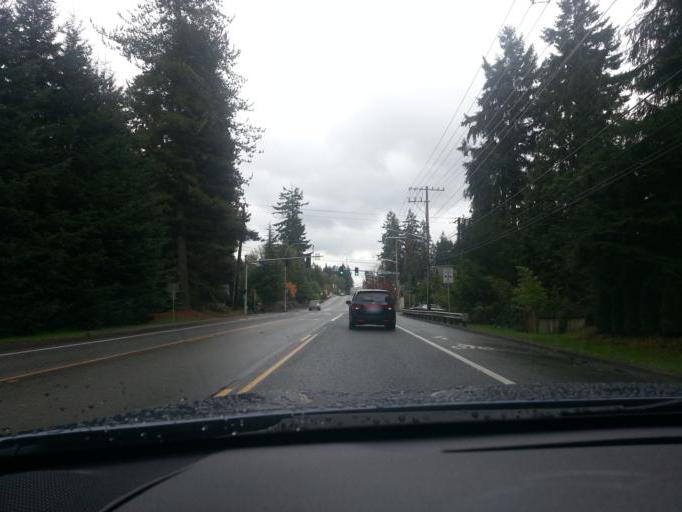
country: US
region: Washington
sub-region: Snohomish County
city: North Creek
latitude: 47.7911
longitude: -122.1876
